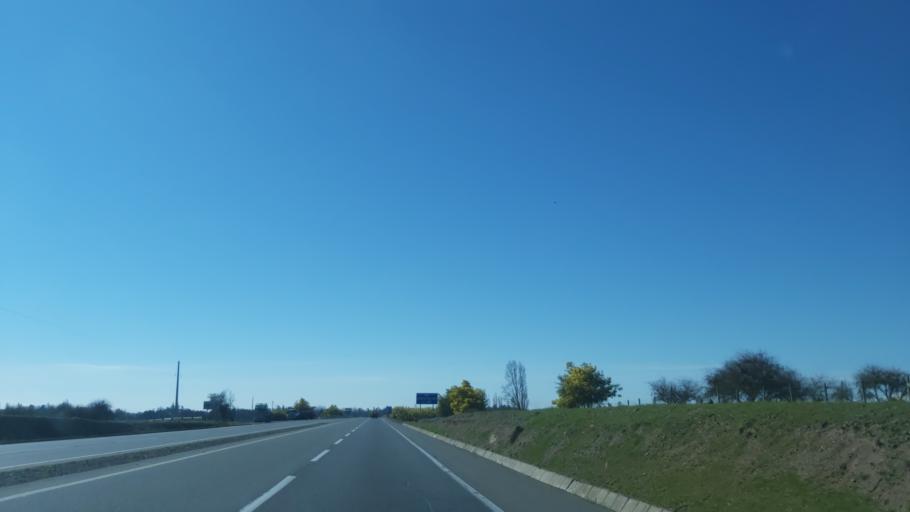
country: CL
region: Biobio
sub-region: Provincia de Nuble
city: Bulnes
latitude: -36.6561
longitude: -72.2446
